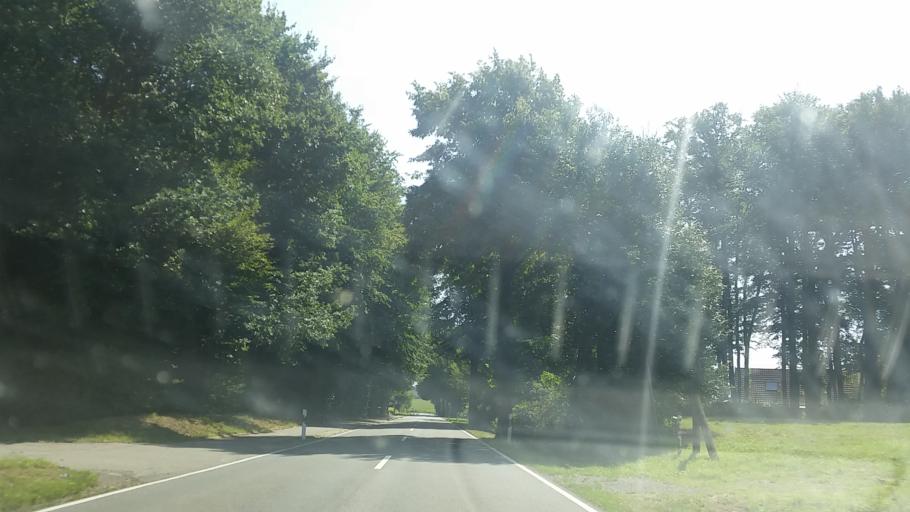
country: DE
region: Lower Saxony
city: Alfhausen
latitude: 52.5053
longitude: 7.9323
